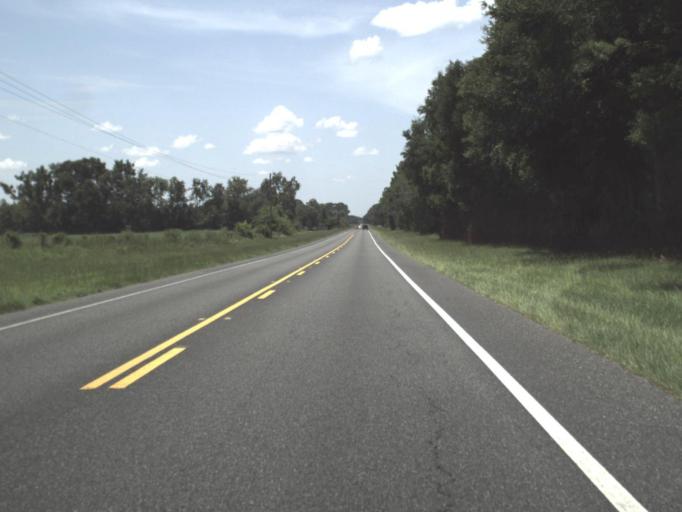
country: US
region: Florida
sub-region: Gilchrist County
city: Trenton
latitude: 29.5678
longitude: -82.8231
